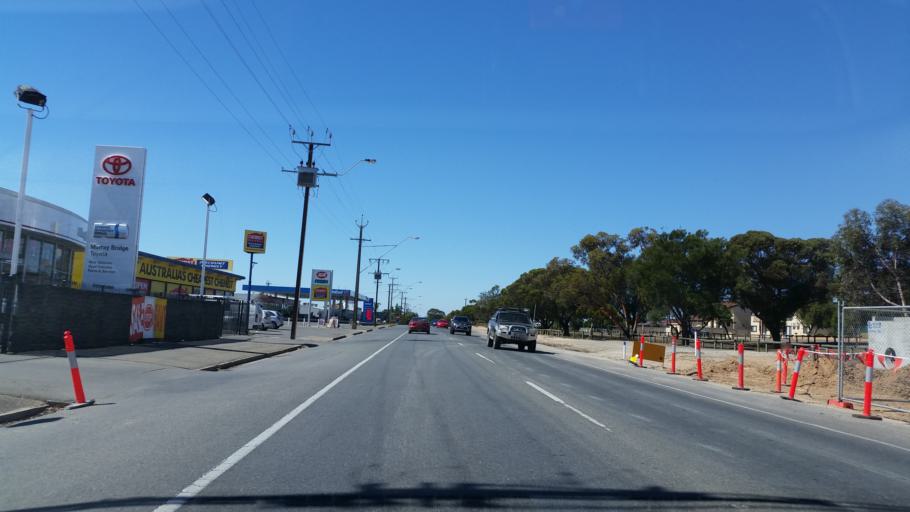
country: AU
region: South Australia
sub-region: Murray Bridge
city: Murray Bridge
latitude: -35.1289
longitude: 139.2518
